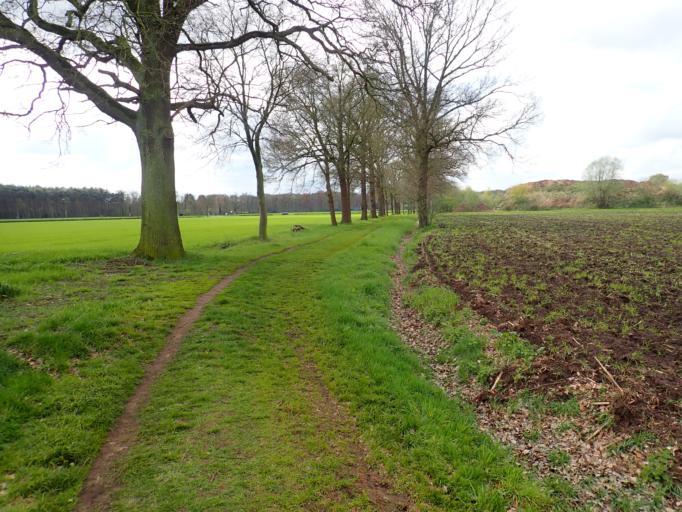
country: BE
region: Flanders
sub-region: Provincie Antwerpen
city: Vorselaar
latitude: 51.2211
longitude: 4.7877
